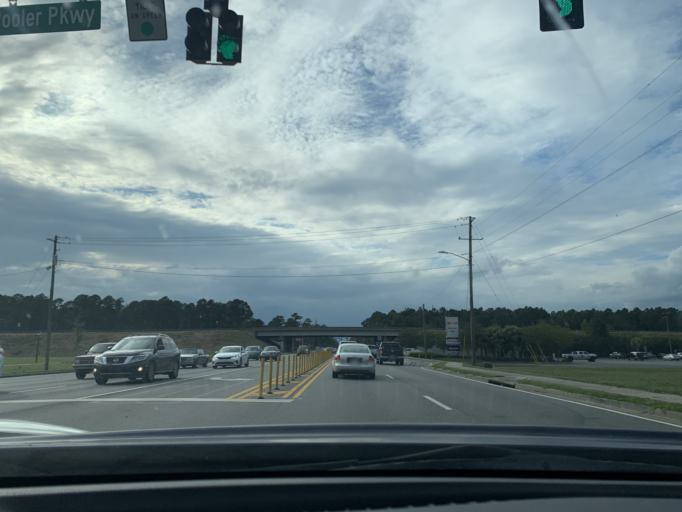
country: US
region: Georgia
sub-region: Chatham County
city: Pooler
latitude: 32.1218
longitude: -81.2657
